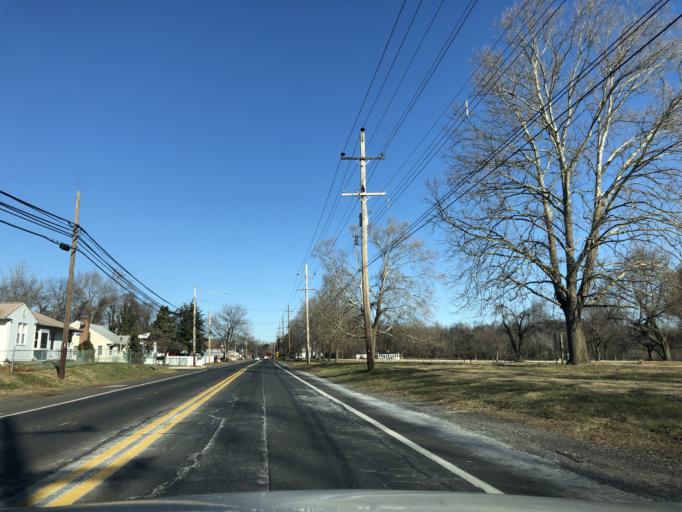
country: US
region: Pennsylvania
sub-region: Bucks County
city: Bristol
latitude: 40.1073
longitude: -74.8644
